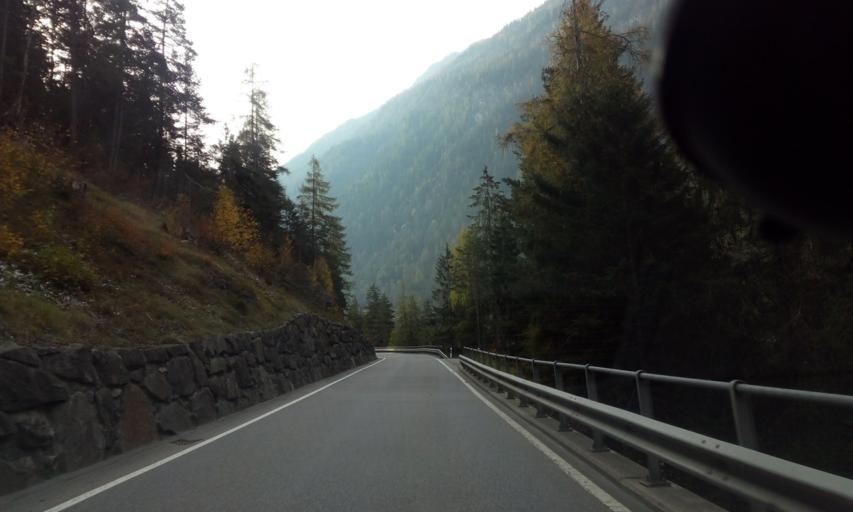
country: CH
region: Grisons
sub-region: Plessur District
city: Arosa
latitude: 46.6656
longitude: 9.6950
